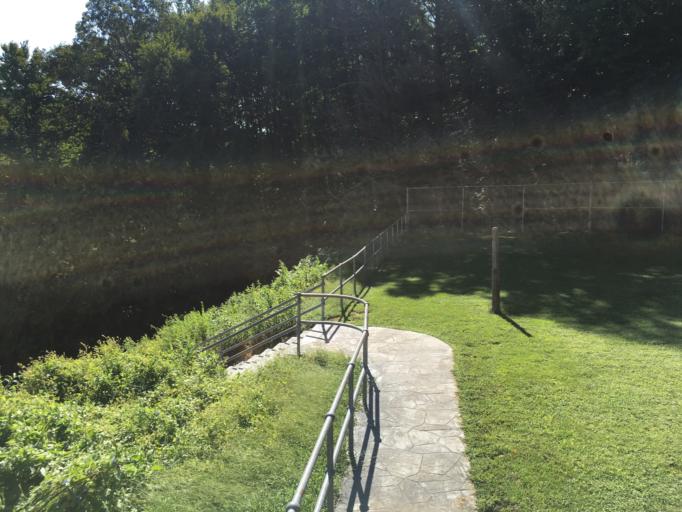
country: US
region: Pennsylvania
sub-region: York County
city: New Freedom
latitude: 39.6189
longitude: -76.7082
